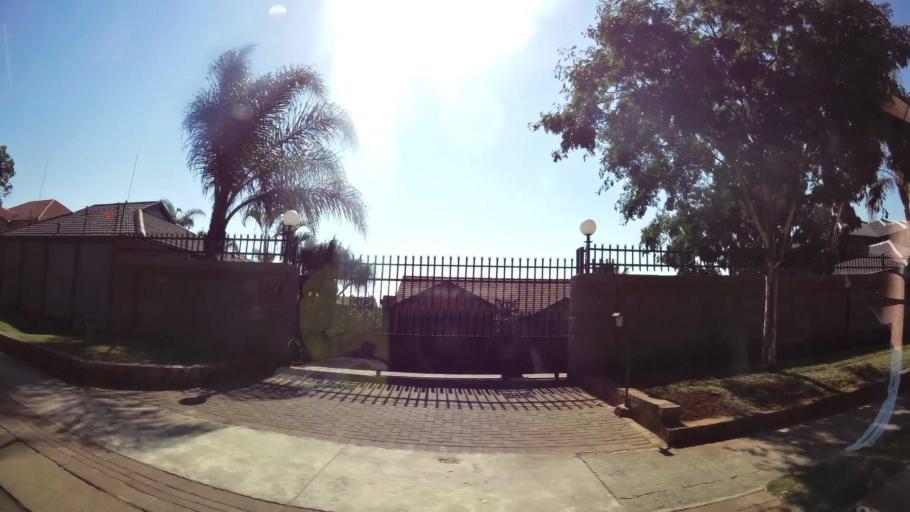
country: ZA
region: Gauteng
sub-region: City of Tshwane Metropolitan Municipality
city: Pretoria
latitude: -25.6866
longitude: 28.2766
